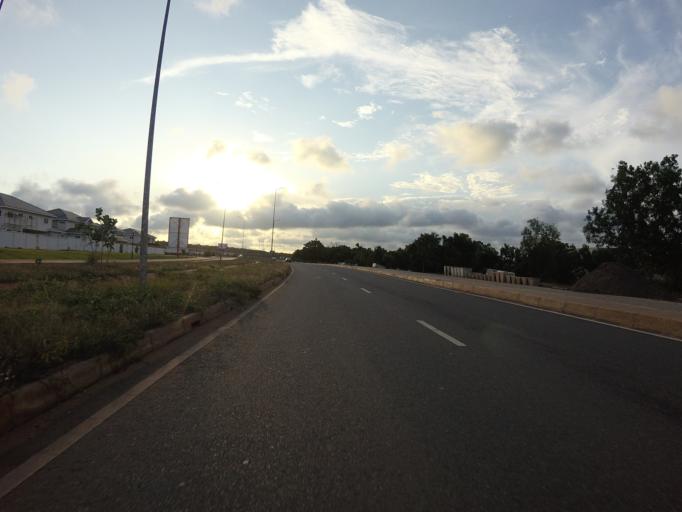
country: GH
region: Greater Accra
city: Teshi Old Town
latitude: 5.6102
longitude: -0.1431
